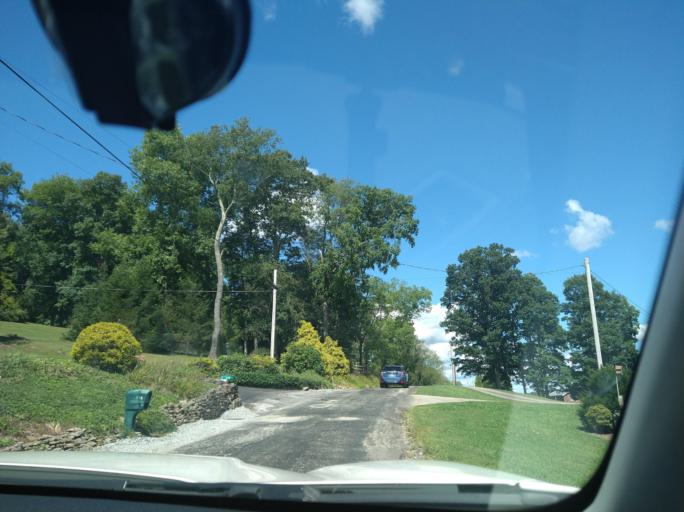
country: US
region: Pennsylvania
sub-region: Fayette County
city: Bear Rocks
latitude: 40.0909
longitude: -79.3665
